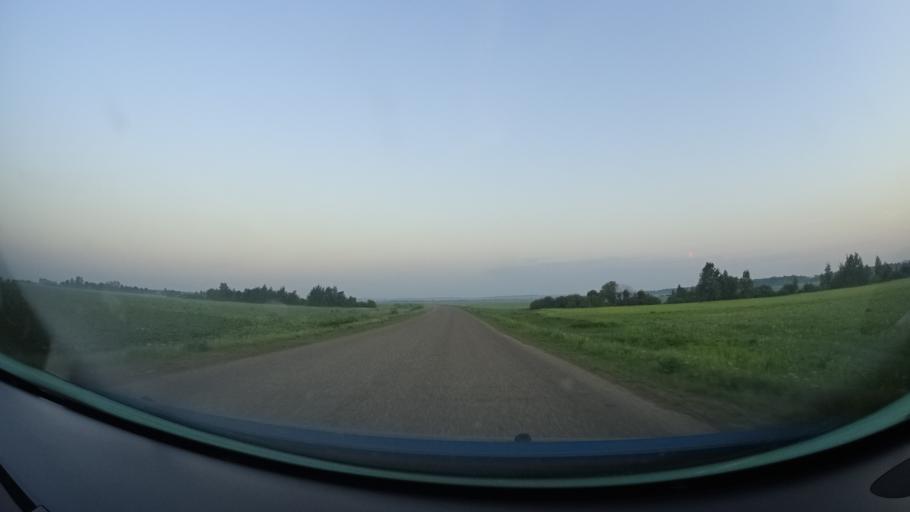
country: RU
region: Bashkortostan
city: Starobaltachevo
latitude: 56.0375
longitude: 55.9388
